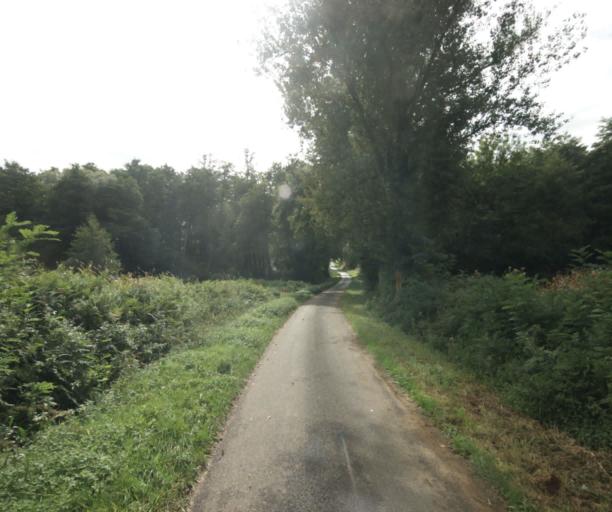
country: FR
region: Midi-Pyrenees
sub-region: Departement du Gers
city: Cazaubon
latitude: 43.9182
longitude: -0.1606
